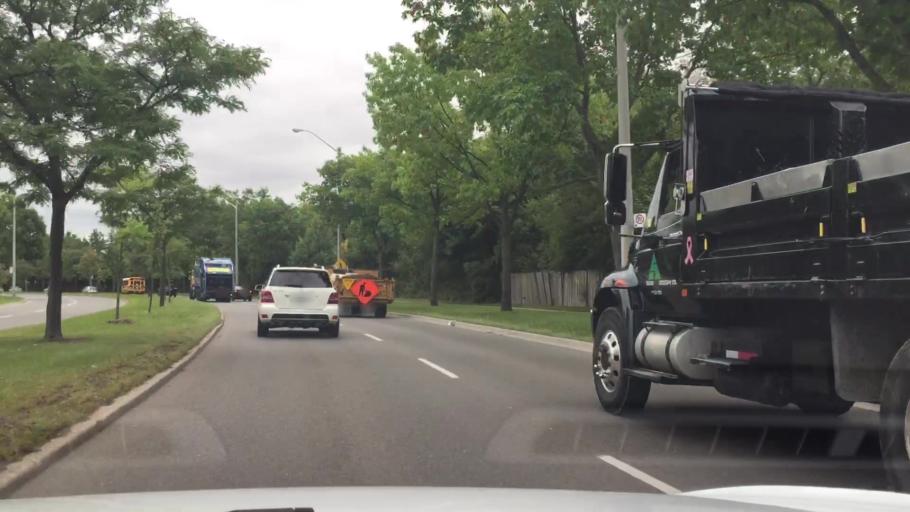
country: CA
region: Ontario
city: Scarborough
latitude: 43.8011
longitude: -79.2183
